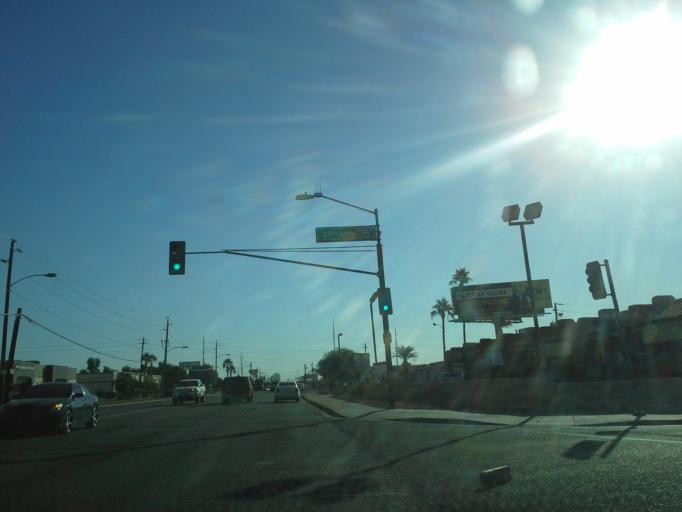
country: US
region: Arizona
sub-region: Maricopa County
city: Phoenix
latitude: 33.4804
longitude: -112.1303
